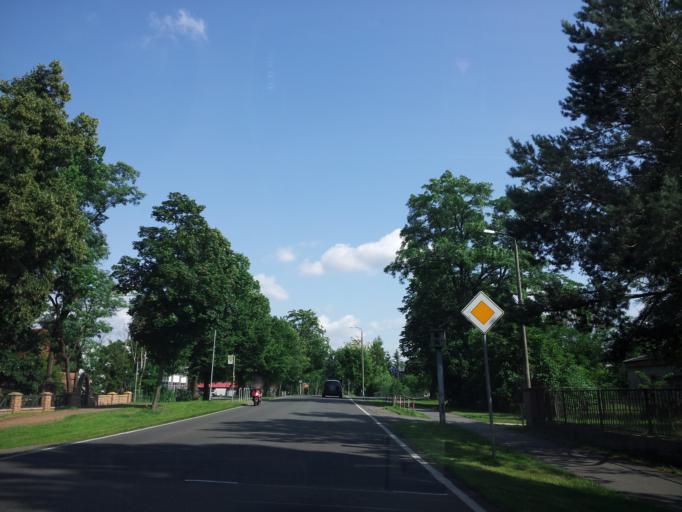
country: DE
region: Brandenburg
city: Niedergorsdorf
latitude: 52.0107
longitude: 13.0071
